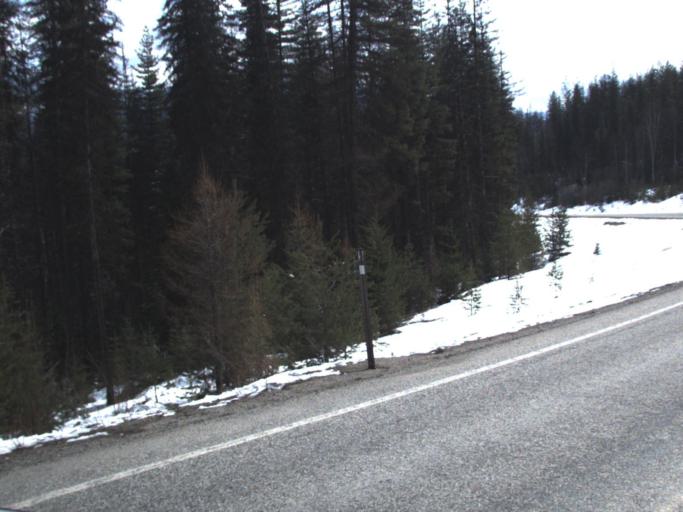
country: CA
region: British Columbia
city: Fruitvale
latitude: 48.6821
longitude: -117.4495
